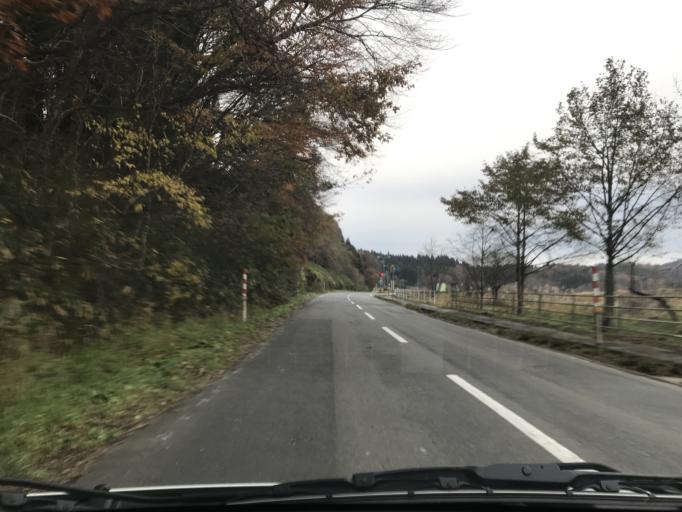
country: JP
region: Iwate
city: Kitakami
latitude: 39.2677
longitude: 141.2680
